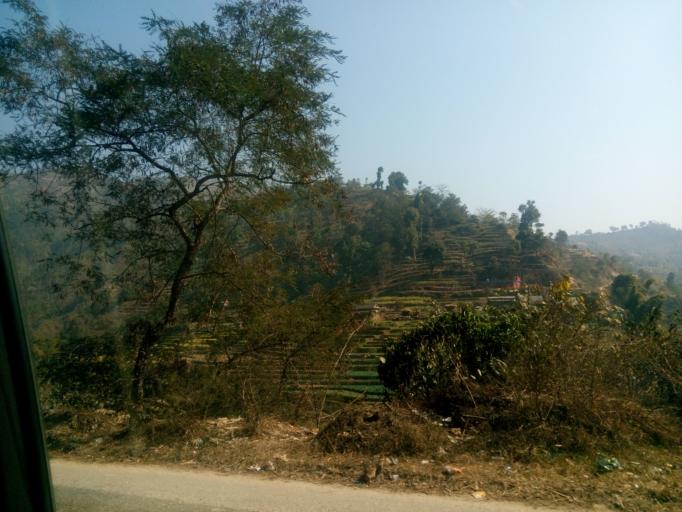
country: NP
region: Central Region
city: Kirtipur
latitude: 27.7586
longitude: 85.0435
